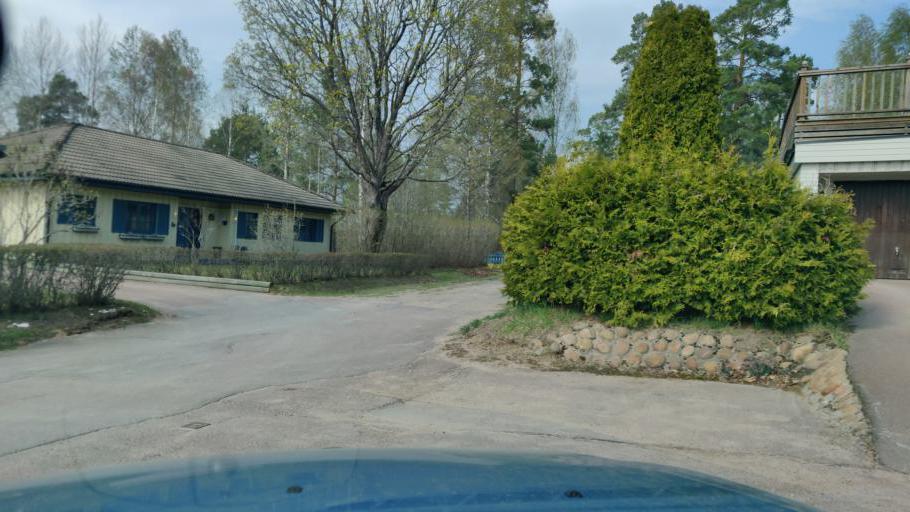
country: SE
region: Vaermland
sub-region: Munkfors Kommun
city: Munkfors
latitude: 59.8455
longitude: 13.5618
